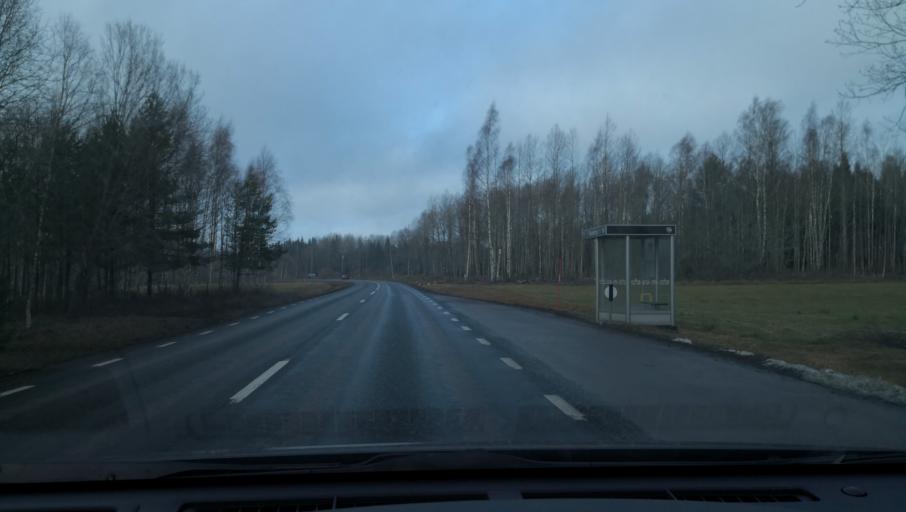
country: SE
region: Vaestra Goetaland
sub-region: Gullspangs Kommun
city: Gullspang
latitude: 58.9516
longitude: 14.0775
